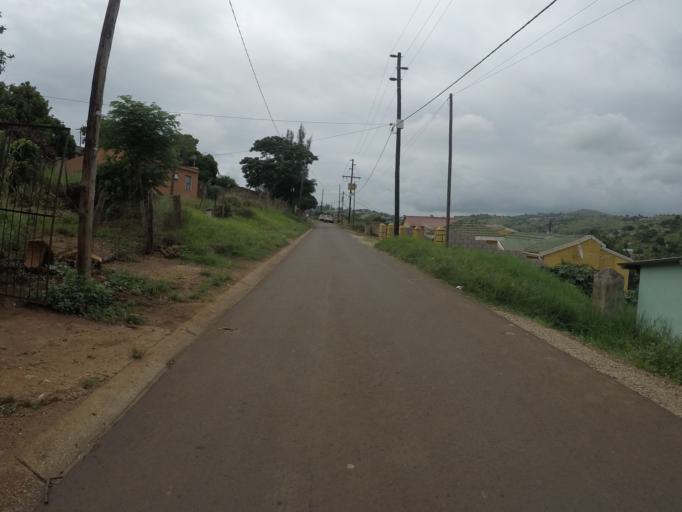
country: ZA
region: KwaZulu-Natal
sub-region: uThungulu District Municipality
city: Empangeni
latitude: -28.7671
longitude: 31.8597
